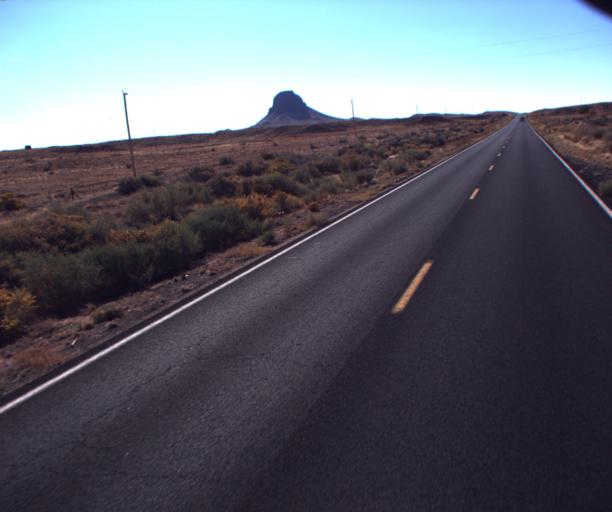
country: US
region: Arizona
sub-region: Navajo County
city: Dilkon
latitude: 35.3275
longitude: -110.4234
